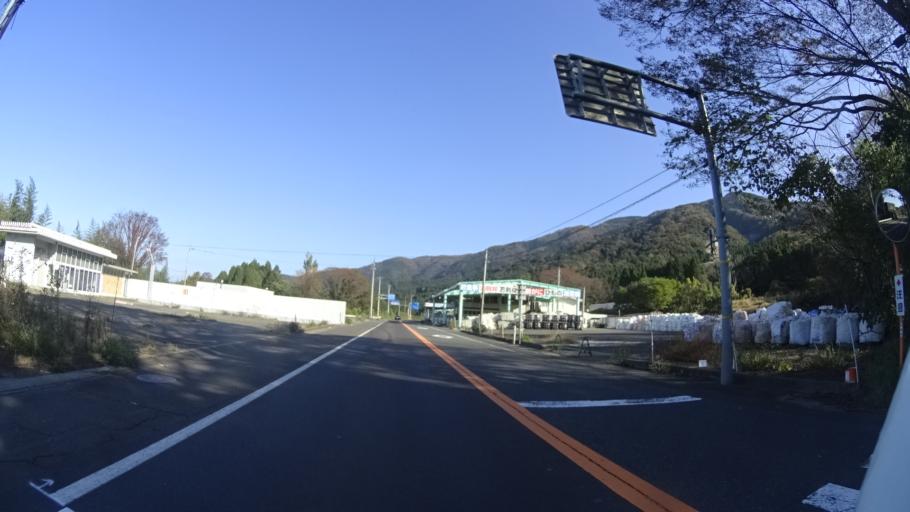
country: JP
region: Fukui
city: Tsuruga
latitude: 35.7406
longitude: 136.1015
